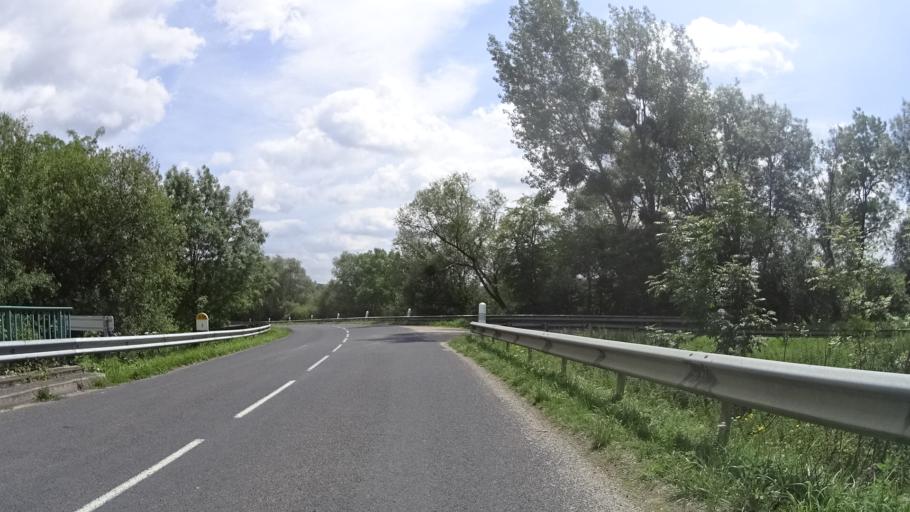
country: FR
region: Lorraine
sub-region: Departement de la Meuse
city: Euville
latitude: 48.7346
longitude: 5.6610
